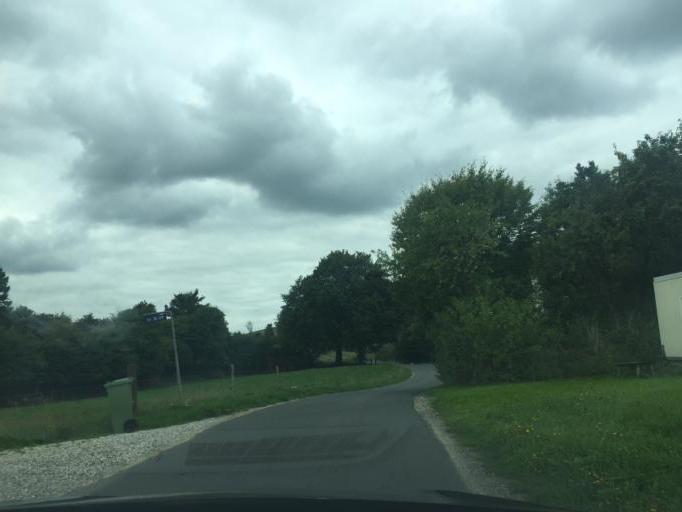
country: DK
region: South Denmark
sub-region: Assens Kommune
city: Tommerup
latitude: 55.3564
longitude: 10.2265
